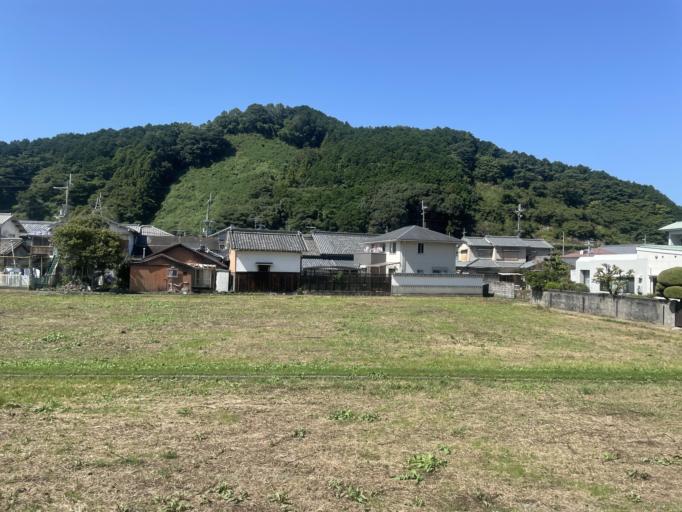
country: JP
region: Nara
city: Gose
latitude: 34.4275
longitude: 135.7567
